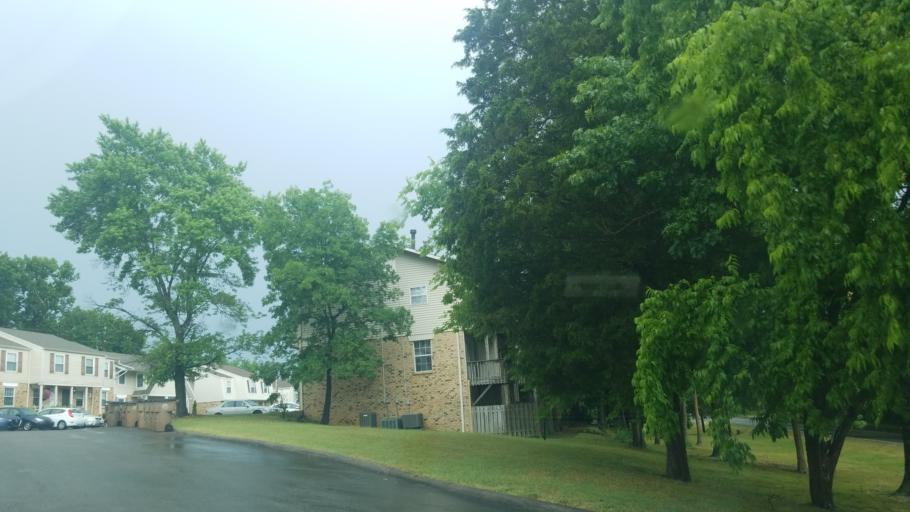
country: US
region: Tennessee
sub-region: Rutherford County
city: La Vergne
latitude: 36.1037
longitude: -86.6039
